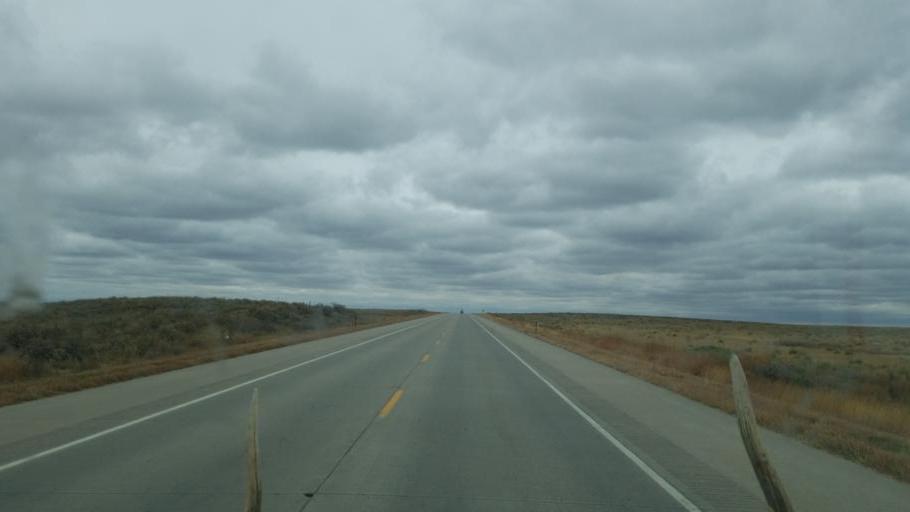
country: US
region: Colorado
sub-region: Kiowa County
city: Eads
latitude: 38.4998
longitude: -102.7857
